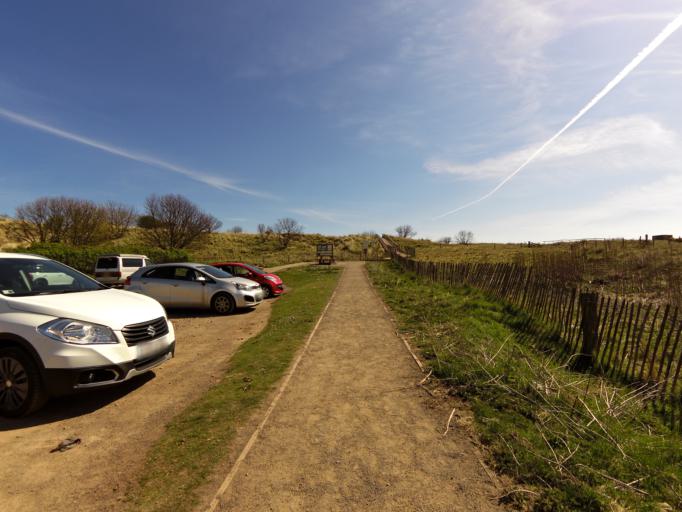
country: GB
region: Scotland
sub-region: Angus
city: Montrose
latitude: 56.6550
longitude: -2.5061
